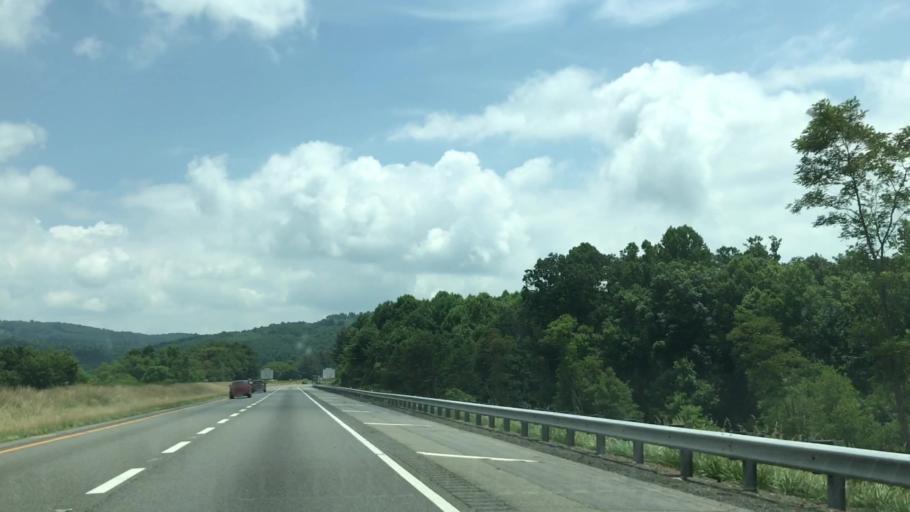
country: US
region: Virginia
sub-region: Carroll County
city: Hillsville
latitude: 36.6822
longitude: -80.7172
